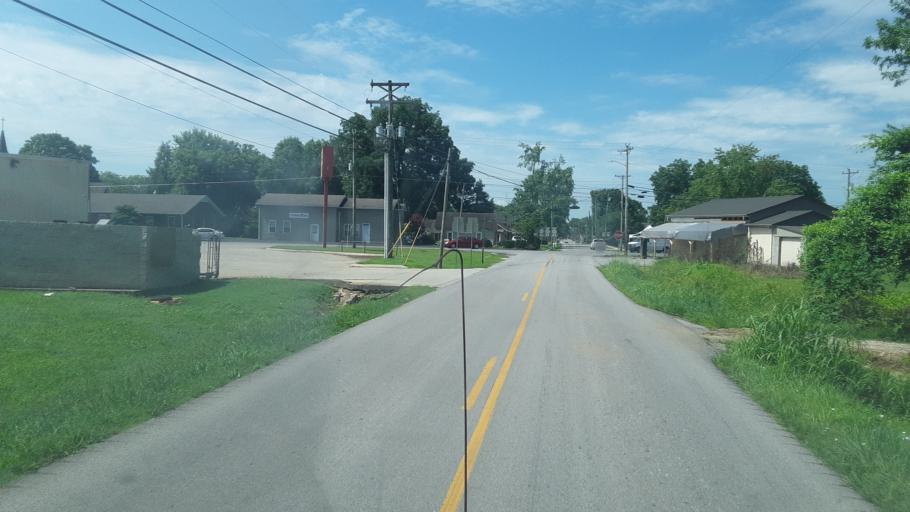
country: US
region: Kentucky
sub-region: Christian County
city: Oak Grove
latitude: 36.7791
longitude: -87.3532
